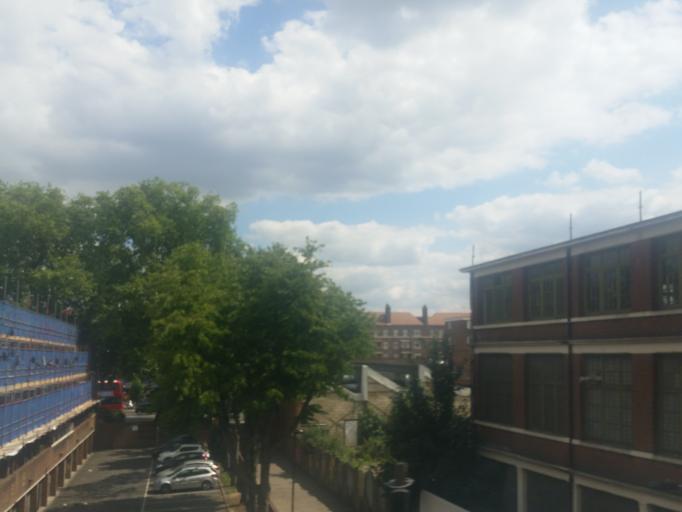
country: GB
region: England
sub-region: Greater London
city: Camberwell
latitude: 51.4774
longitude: -0.0954
